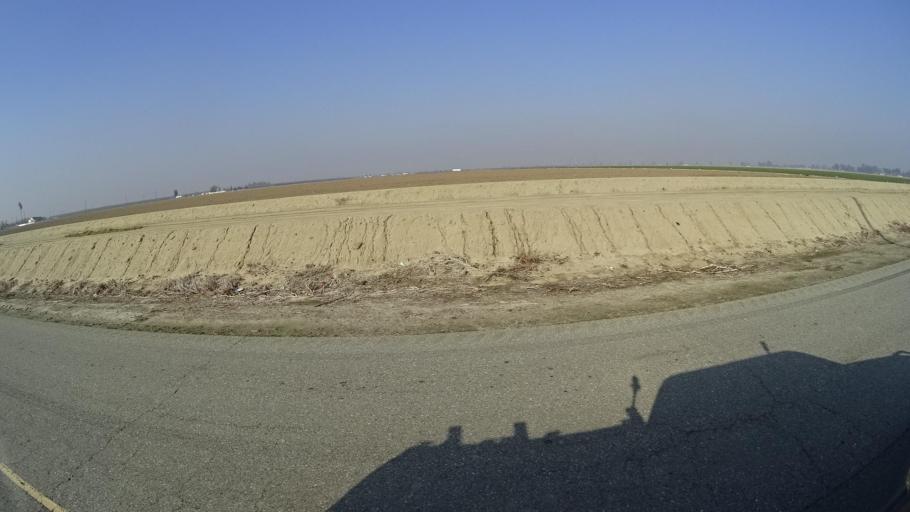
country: US
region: California
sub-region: Kern County
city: Greenfield
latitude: 35.2233
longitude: -119.0357
